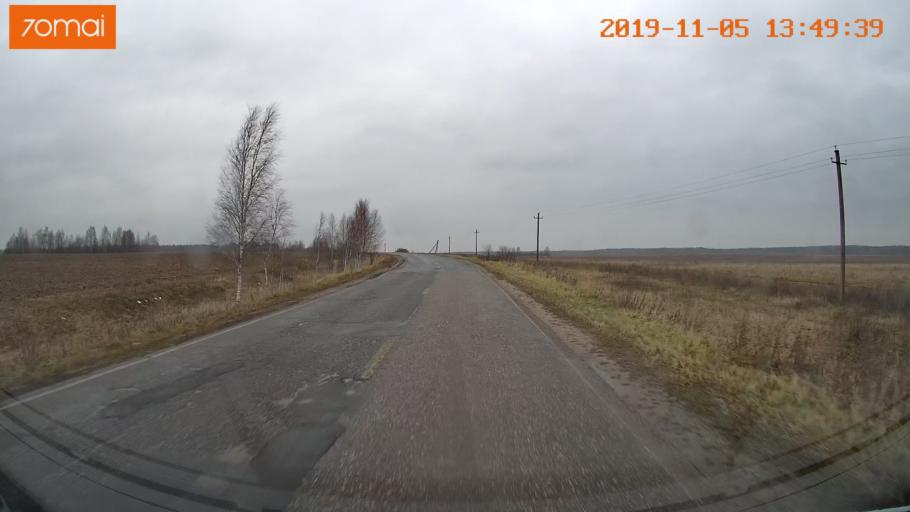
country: RU
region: Ivanovo
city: Kaminskiy
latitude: 57.0136
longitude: 41.4105
